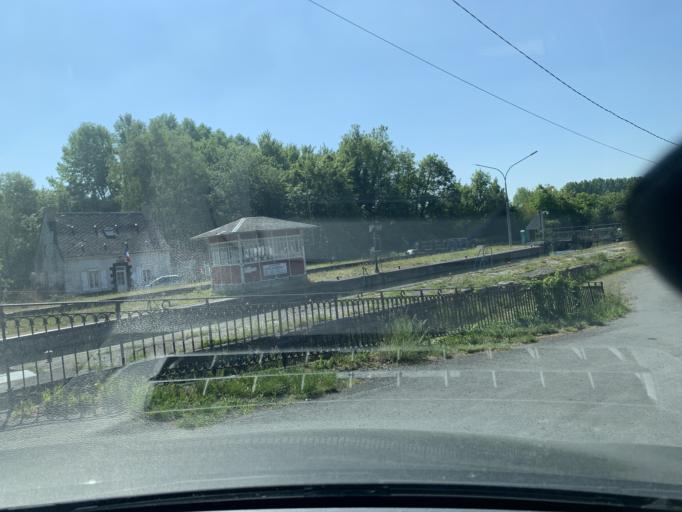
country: FR
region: Nord-Pas-de-Calais
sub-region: Departement du Nord
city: Proville
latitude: 50.1545
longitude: 3.1845
